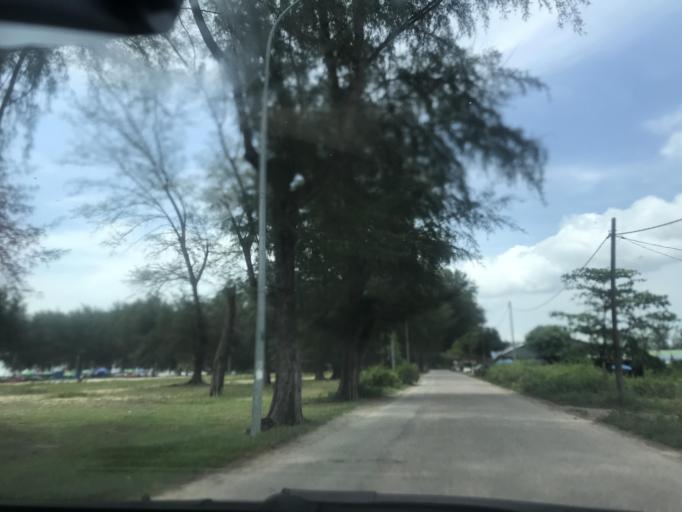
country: MY
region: Kelantan
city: Tumpat
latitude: 6.2235
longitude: 102.1180
